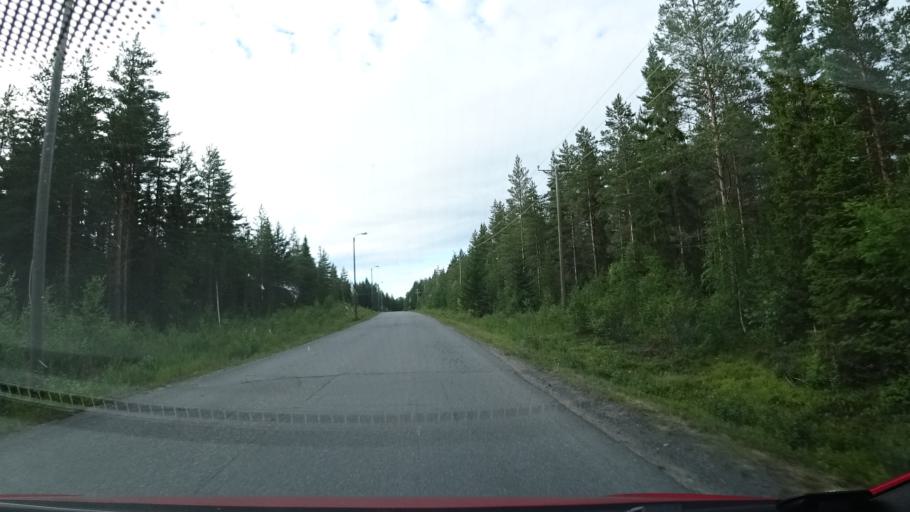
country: FI
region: Northern Ostrobothnia
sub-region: Oulu
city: Haukipudas
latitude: 65.1985
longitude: 25.4134
